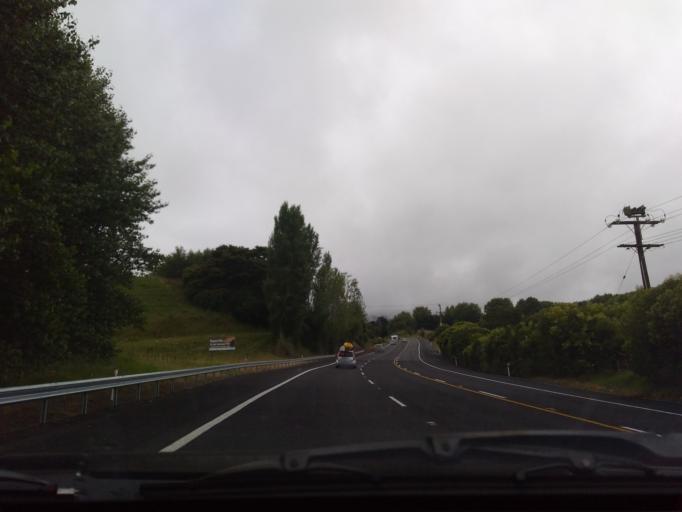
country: NZ
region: Auckland
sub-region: Auckland
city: Wellsford
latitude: -36.1525
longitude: 174.4388
